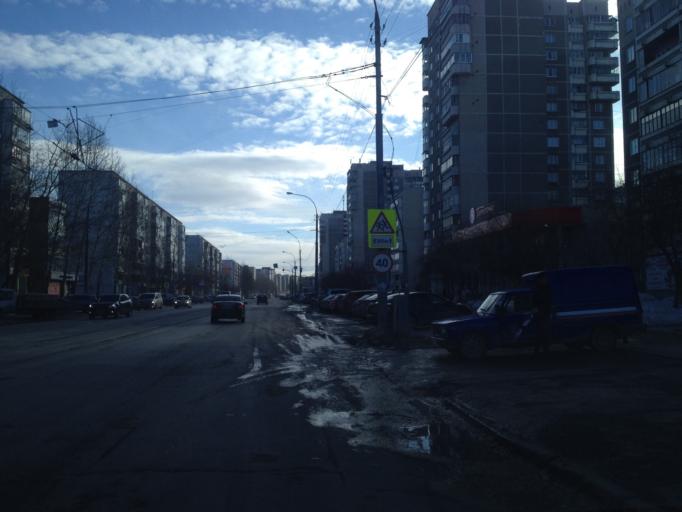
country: RU
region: Sverdlovsk
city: Yekaterinburg
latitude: 56.8349
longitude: 60.5455
